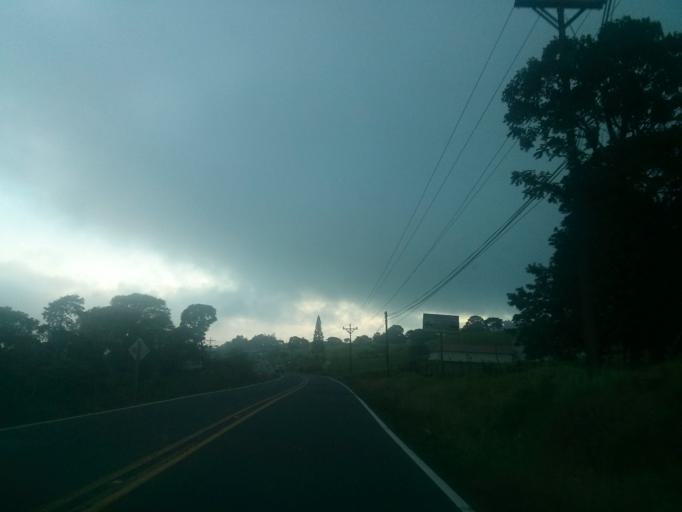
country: CR
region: Cartago
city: Cot
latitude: 9.8894
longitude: -83.8586
